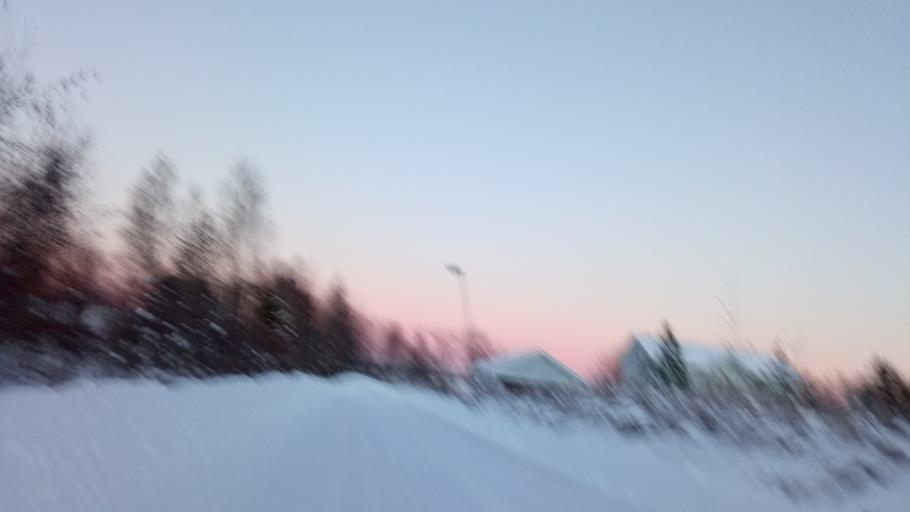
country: FI
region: Southern Ostrobothnia
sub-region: Jaerviseutu
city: Alajaervi
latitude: 62.9902
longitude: 23.8568
